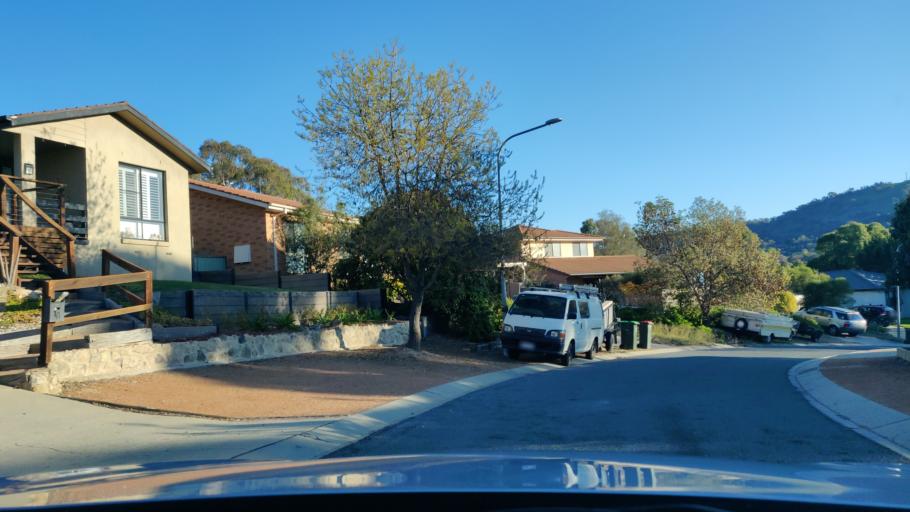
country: AU
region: Australian Capital Territory
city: Macarthur
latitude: -35.4445
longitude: 149.1277
